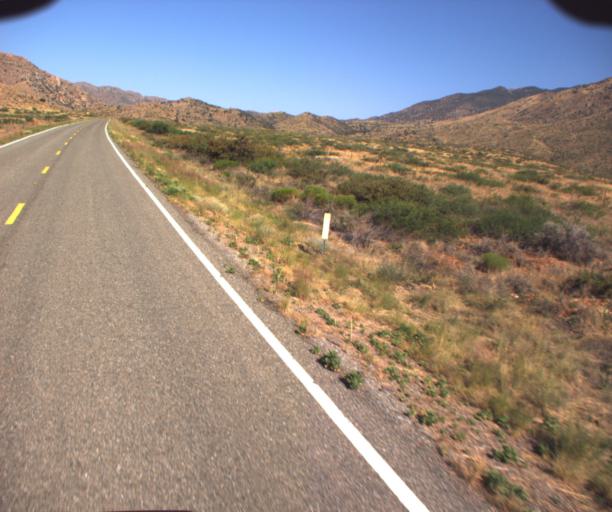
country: US
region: Arizona
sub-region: Graham County
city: Swift Trail Junction
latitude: 32.5605
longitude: -109.7708
